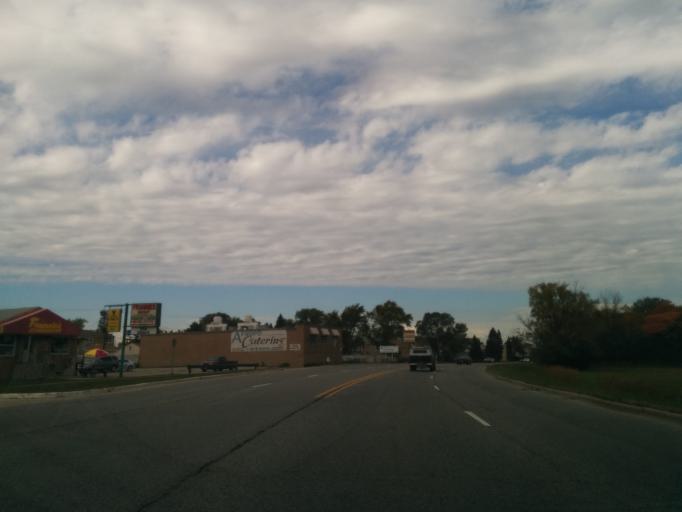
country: US
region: Illinois
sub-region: Cook County
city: Schiller Park
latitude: 41.9571
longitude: -87.8605
